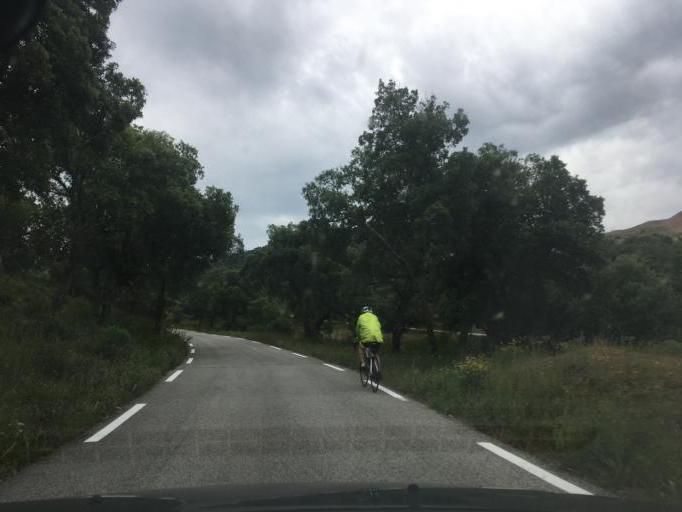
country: FR
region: Provence-Alpes-Cote d'Azur
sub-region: Departement du Var
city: Pierrefeu-du-Var
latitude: 43.2309
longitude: 6.2131
